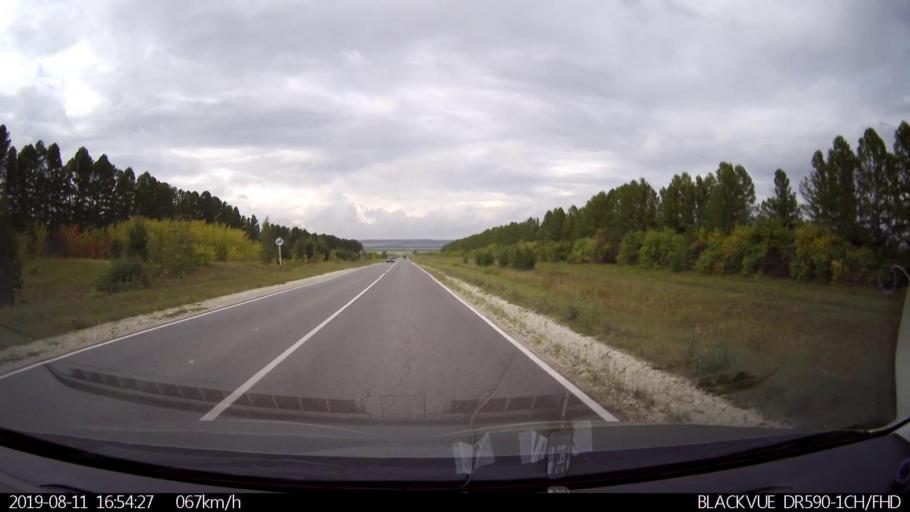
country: RU
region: Ulyanovsk
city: Mayna
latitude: 54.2727
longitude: 47.6664
